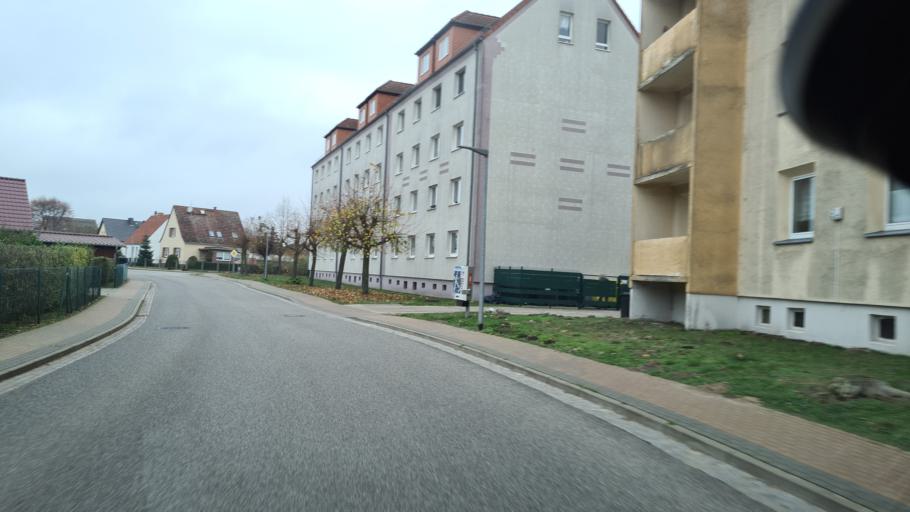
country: DE
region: Brandenburg
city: Lindow
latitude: 52.9661
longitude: 12.9886
